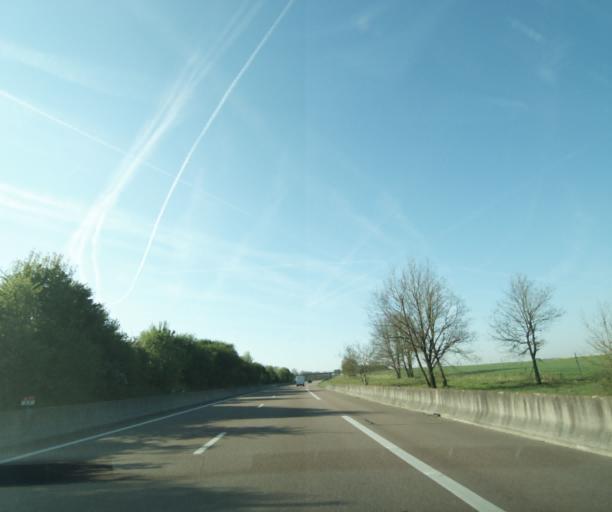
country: FR
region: Ile-de-France
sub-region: Departement de Seine-et-Marne
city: Souppes-sur-Loing
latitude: 48.2105
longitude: 2.7748
